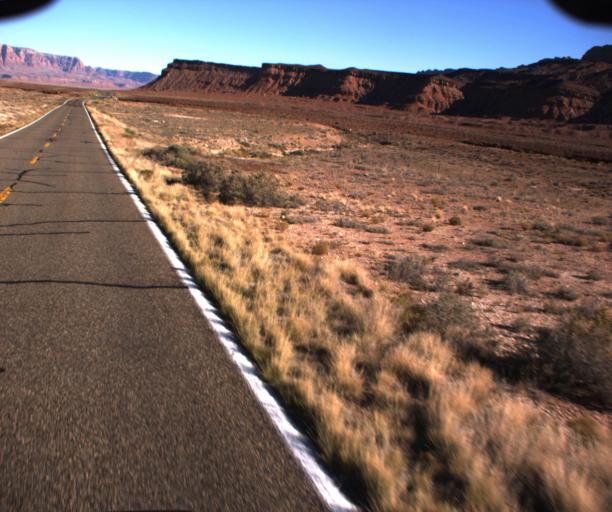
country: US
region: Arizona
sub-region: Coconino County
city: LeChee
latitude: 36.6895
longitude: -111.6552
